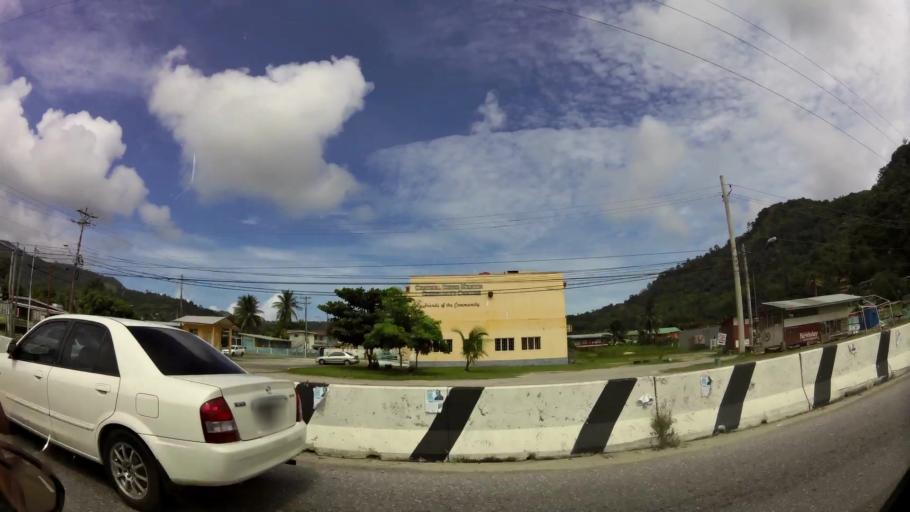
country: TT
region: Diego Martin
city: Petit Valley
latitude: 10.7177
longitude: -61.5556
